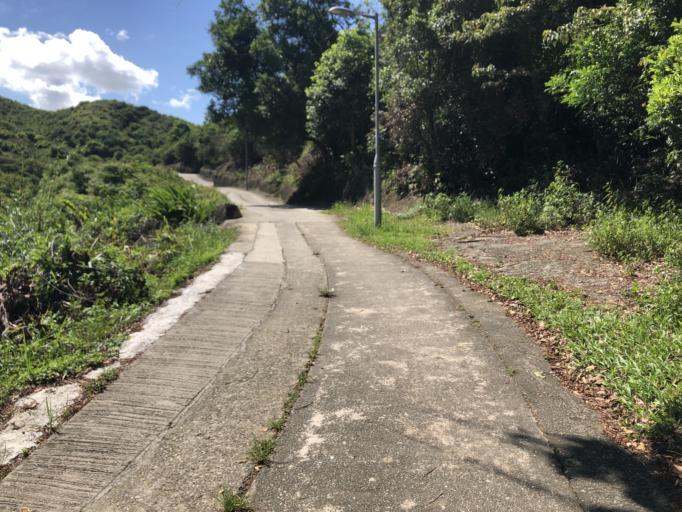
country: HK
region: Tuen Mun
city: Tuen Mun
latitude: 22.2921
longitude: 113.9767
